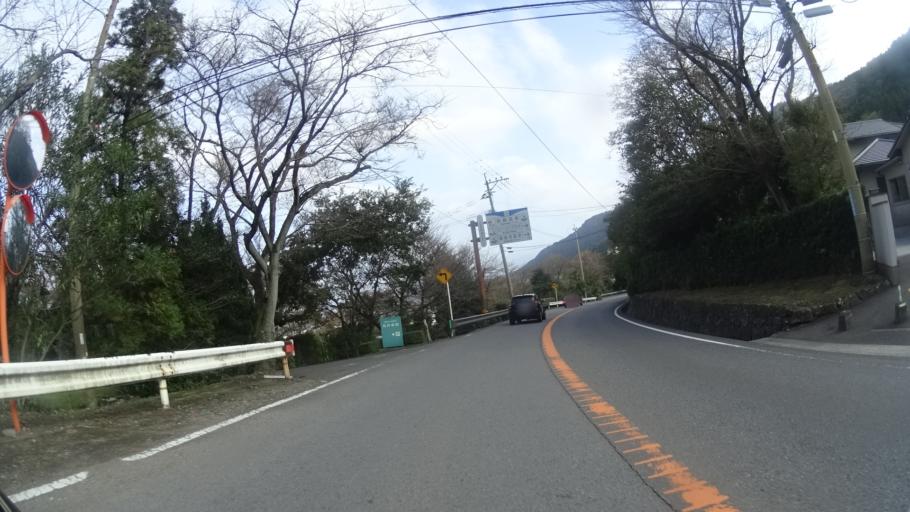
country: JP
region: Oita
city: Beppu
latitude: 33.2903
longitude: 131.4580
